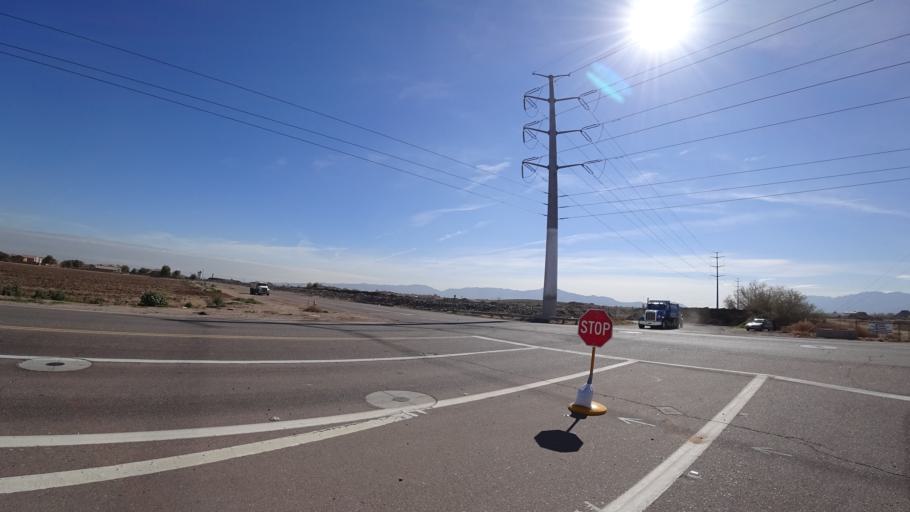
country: US
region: Arizona
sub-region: Maricopa County
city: Laveen
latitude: 33.4083
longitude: -112.1866
